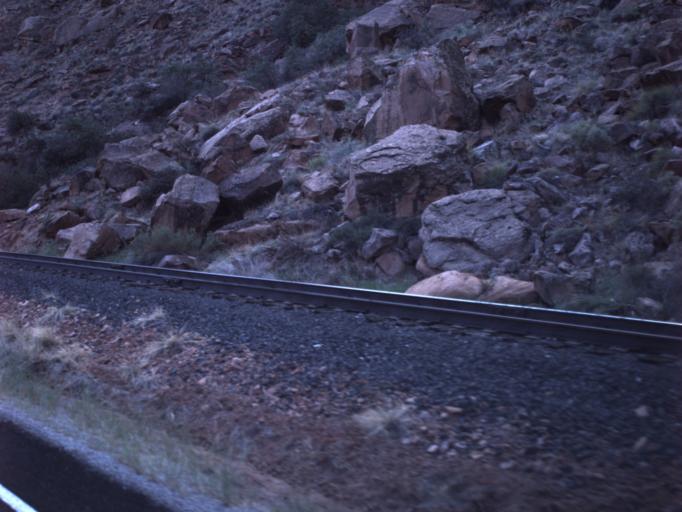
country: US
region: Utah
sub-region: Grand County
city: Moab
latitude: 38.5615
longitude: -109.6583
